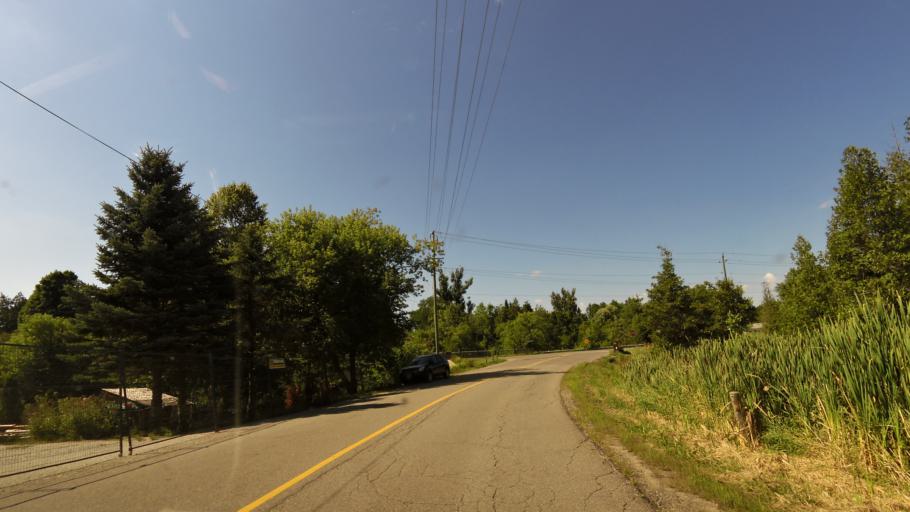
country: CA
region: Ontario
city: Brampton
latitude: 43.7729
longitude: -79.9259
